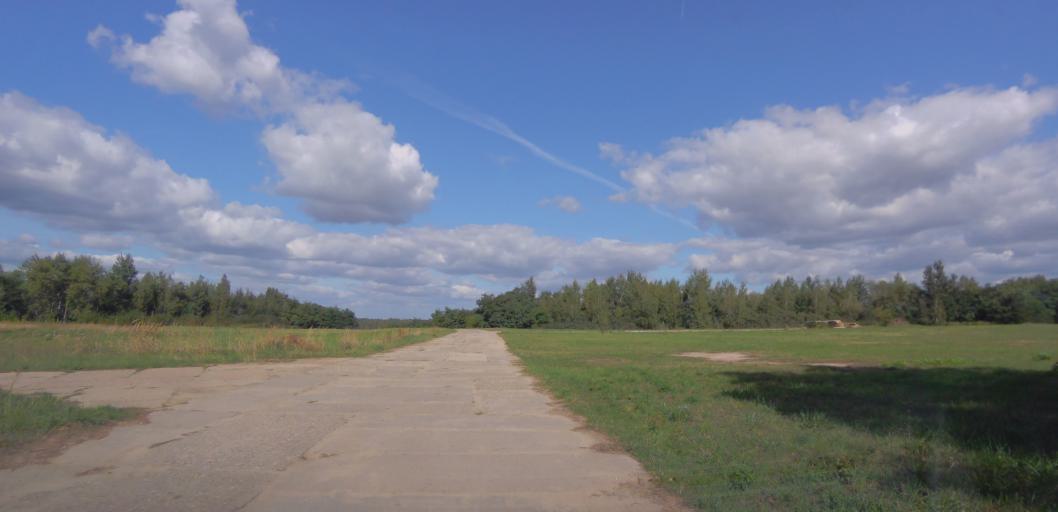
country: PL
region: Subcarpathian Voivodeship
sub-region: Tarnobrzeg
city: Tarnobrzeg
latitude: 50.5348
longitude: 21.6572
